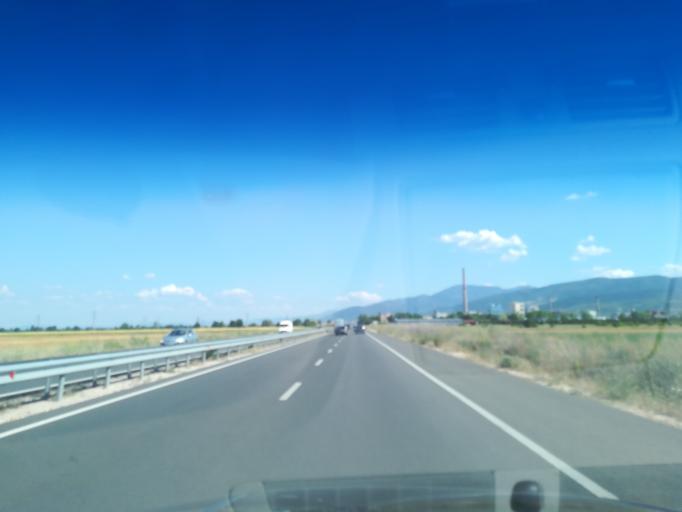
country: BG
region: Plovdiv
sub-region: Obshtina Asenovgrad
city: Asenovgrad
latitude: 42.0733
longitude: 24.8085
